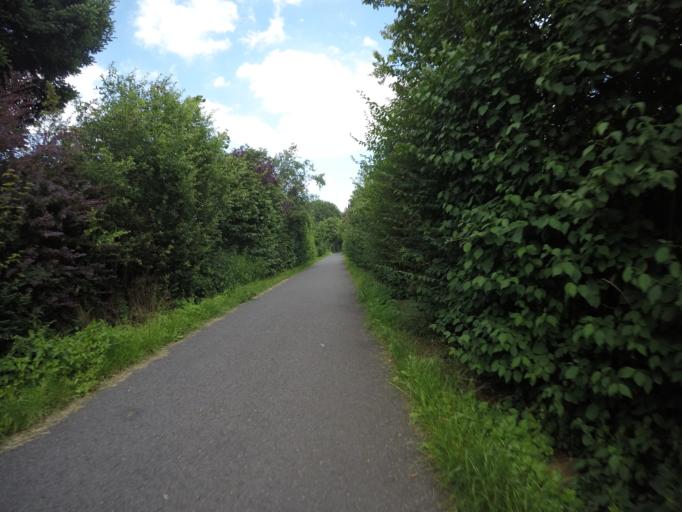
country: DE
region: North Rhine-Westphalia
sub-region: Regierungsbezirk Munster
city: Borken
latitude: 51.8471
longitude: 6.8422
